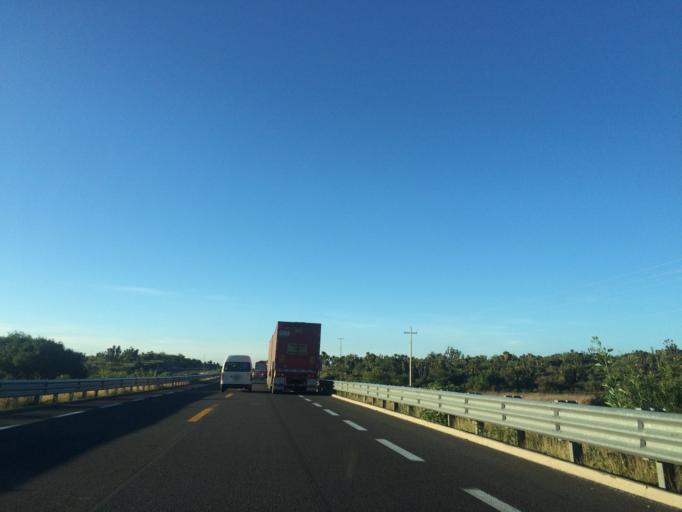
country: MX
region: Puebla
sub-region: Tehuacan
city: Magdalena Cuayucatepec
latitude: 18.5861
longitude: -97.4683
